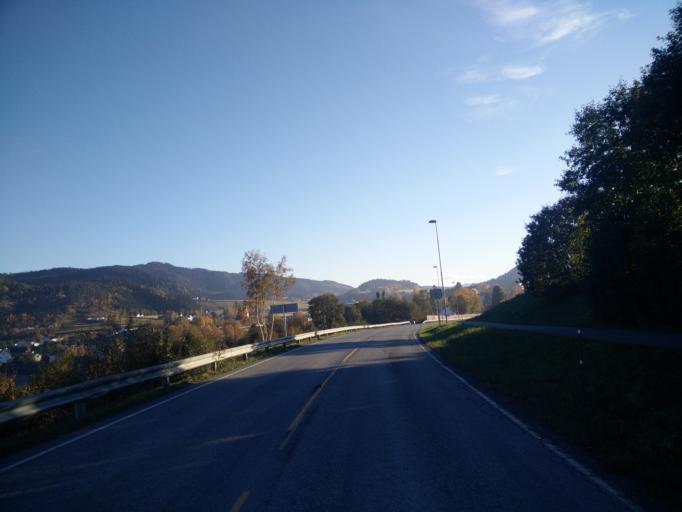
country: NO
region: Sor-Trondelag
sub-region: Skaun
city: Borsa
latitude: 63.3304
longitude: 10.0699
